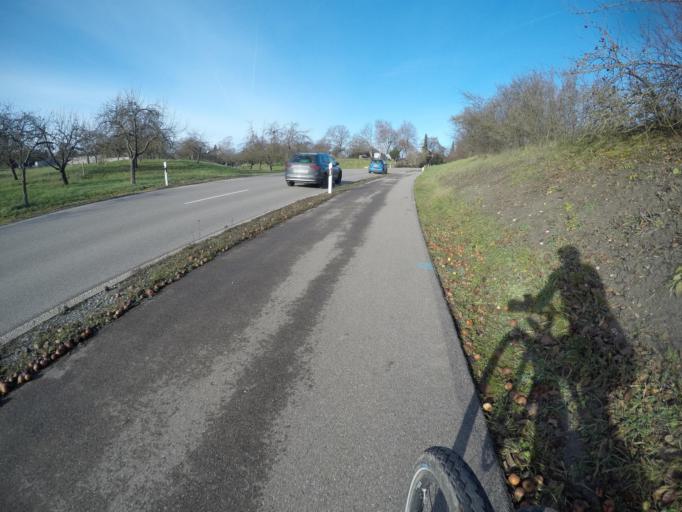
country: DE
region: Baden-Wuerttemberg
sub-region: Regierungsbezirk Stuttgart
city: Korb
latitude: 48.8504
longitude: 9.3558
